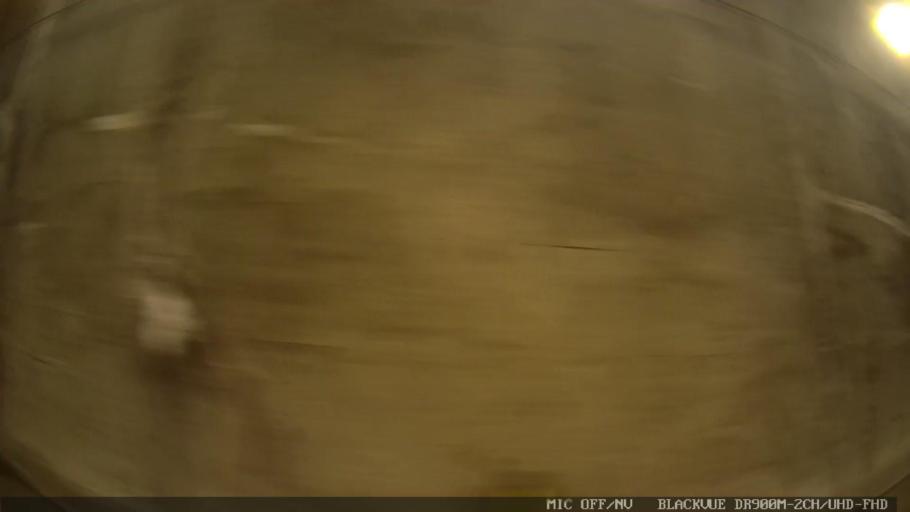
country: BR
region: Sao Paulo
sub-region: Cubatao
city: Cubatao
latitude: -23.8830
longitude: -46.4925
